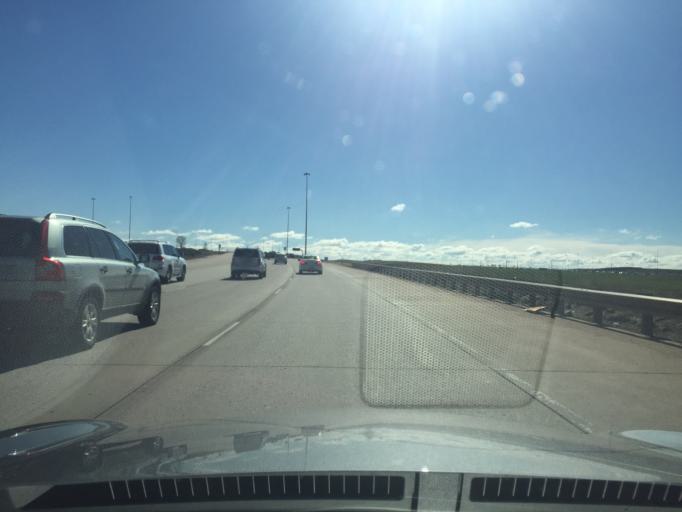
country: US
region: Colorado
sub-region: Adams County
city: Aurora
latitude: 39.8332
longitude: -104.7213
